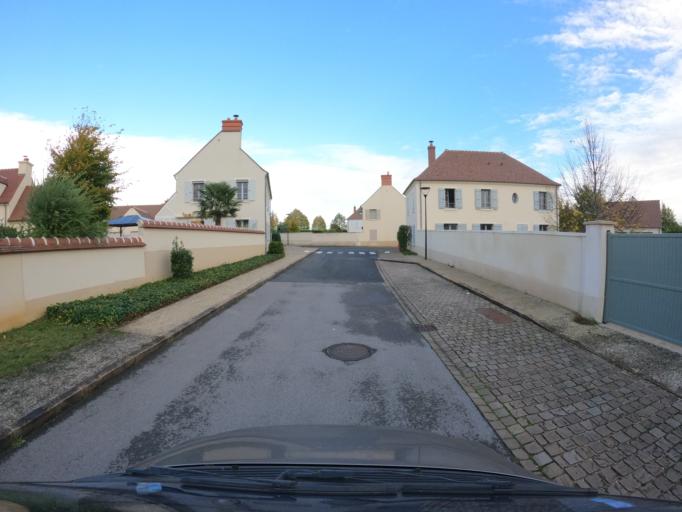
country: FR
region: Ile-de-France
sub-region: Departement de Seine-et-Marne
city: Magny-le-Hongre
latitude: 48.8780
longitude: 2.8117
